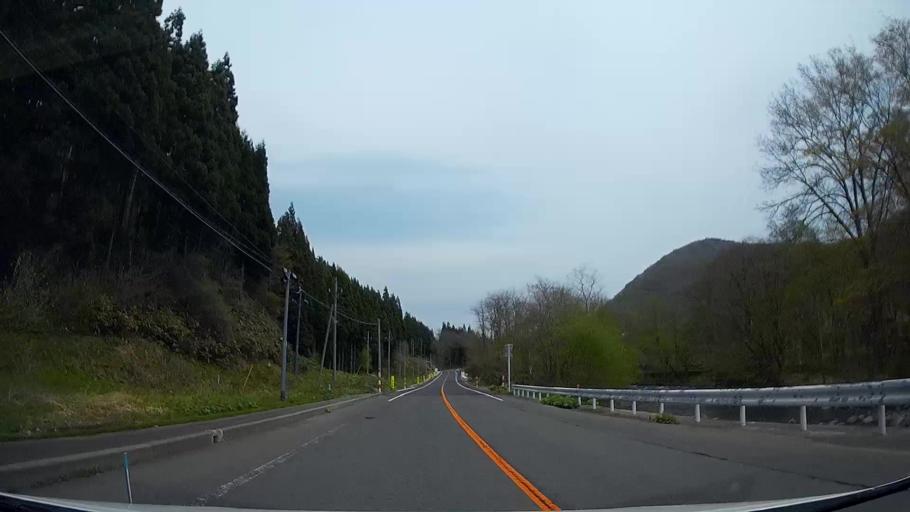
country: JP
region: Akita
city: Hanawa
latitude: 40.3619
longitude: 140.8525
